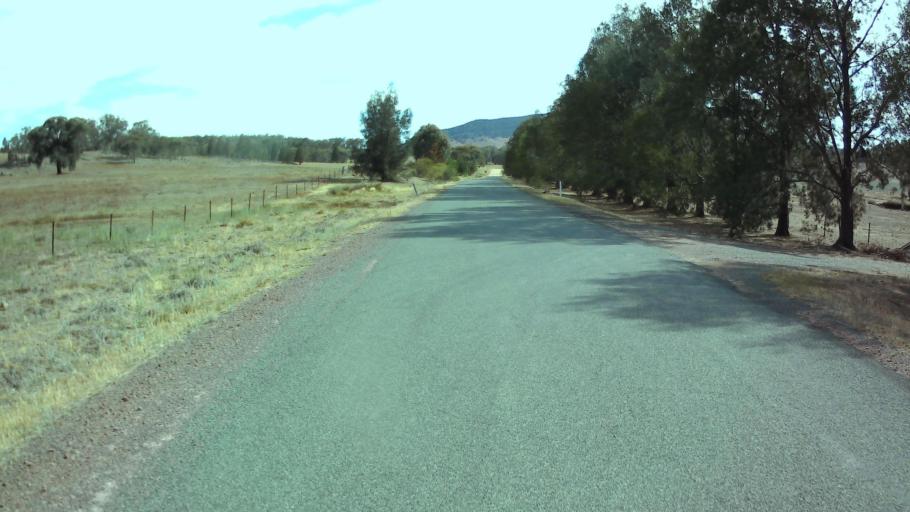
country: AU
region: New South Wales
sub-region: Weddin
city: Grenfell
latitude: -33.8102
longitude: 148.2930
